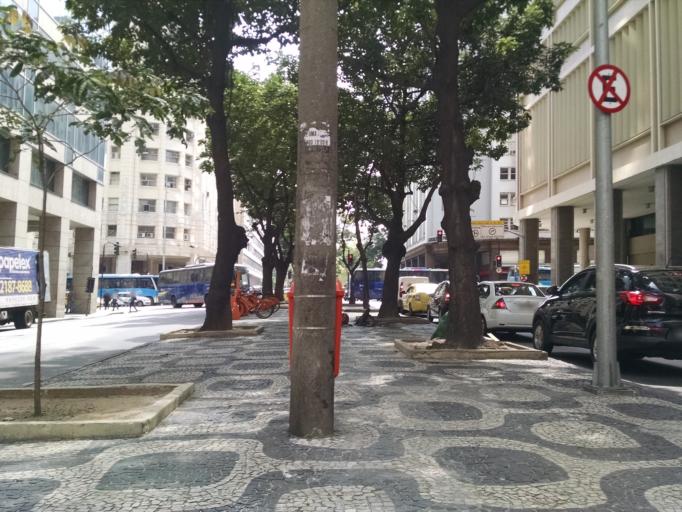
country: BR
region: Rio de Janeiro
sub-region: Rio De Janeiro
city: Rio de Janeiro
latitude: -22.9077
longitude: -43.1756
